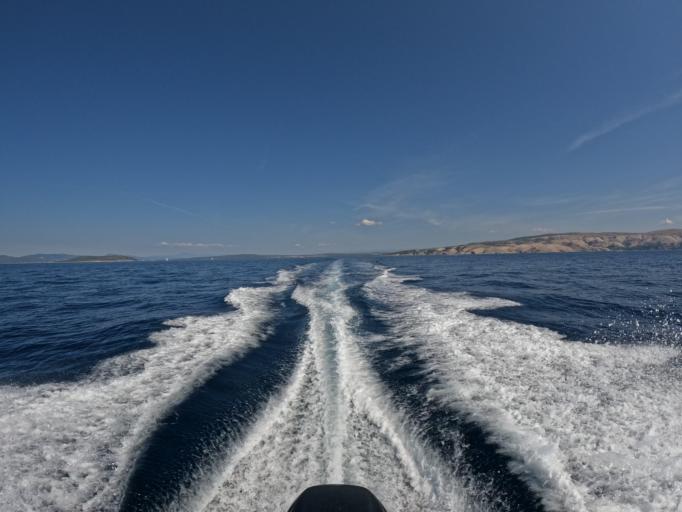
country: HR
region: Primorsko-Goranska
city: Punat
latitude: 44.9226
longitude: 14.6207
